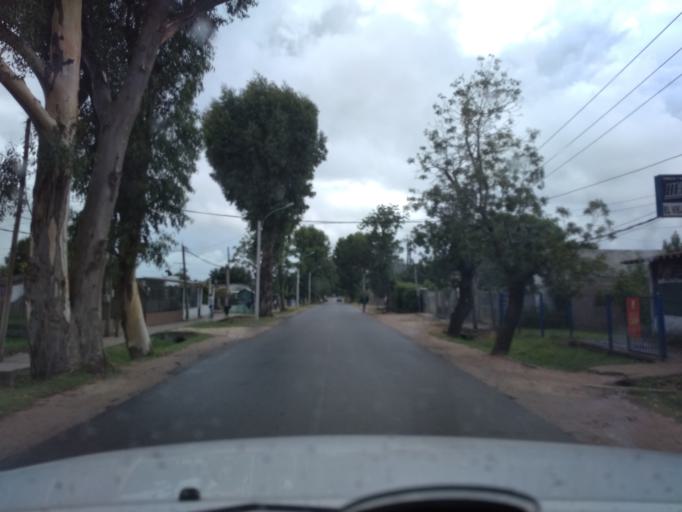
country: UY
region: Canelones
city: Pando
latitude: -34.7125
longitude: -55.9676
